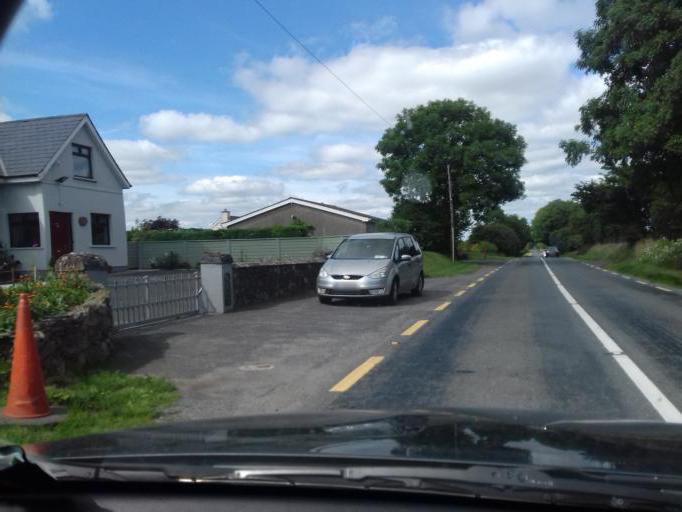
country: IE
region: Leinster
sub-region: Wicklow
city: Valleymount
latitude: 53.0686
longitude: -6.6179
